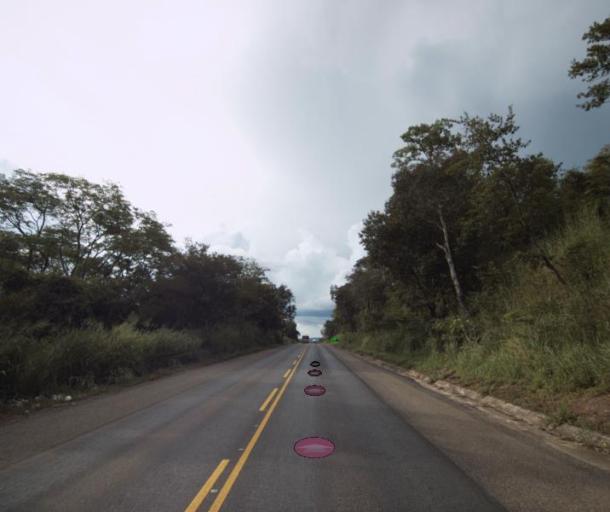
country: BR
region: Goias
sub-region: Ceres
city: Ceres
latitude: -15.1903
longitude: -49.5450
